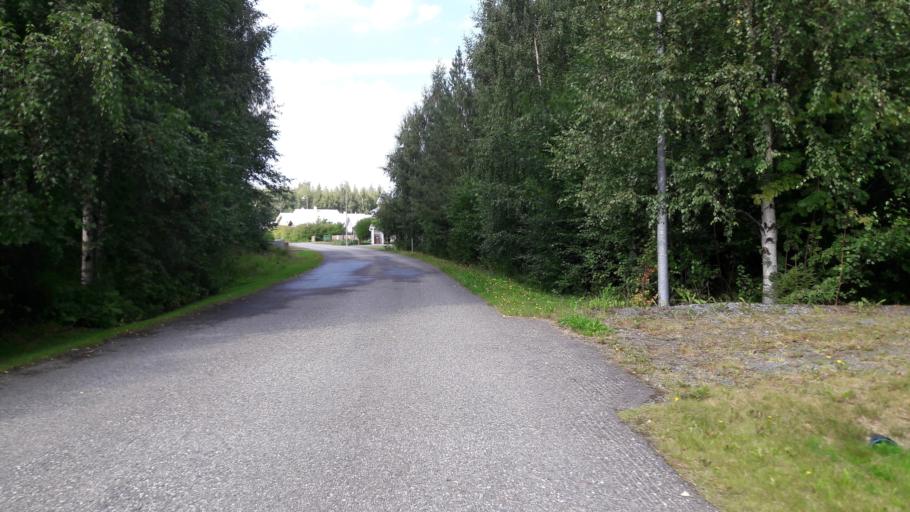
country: FI
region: North Karelia
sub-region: Joensuu
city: Joensuu
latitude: 62.5107
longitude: 29.8275
